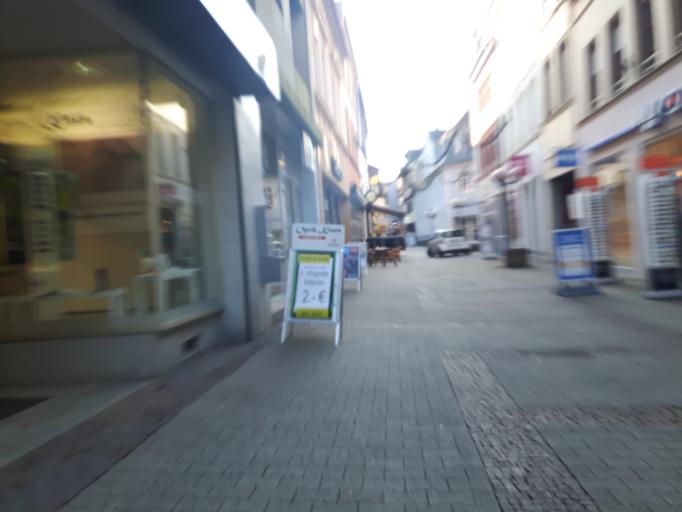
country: DE
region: Rheinland-Pfalz
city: Alzey
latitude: 49.7469
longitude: 8.1129
